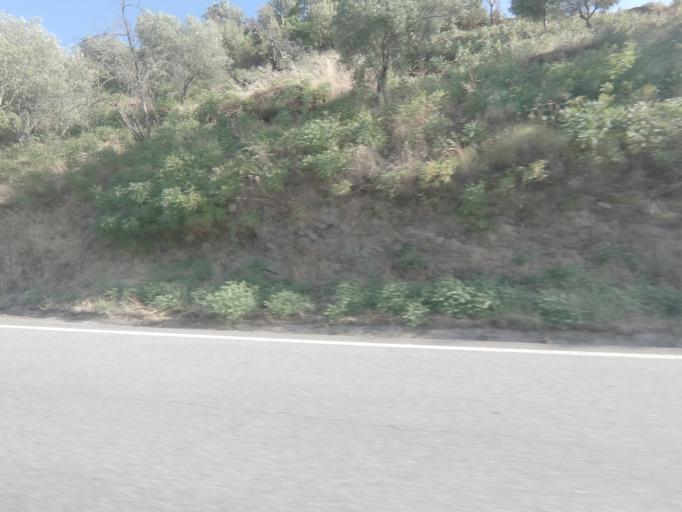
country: PT
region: Viseu
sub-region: Tabuaco
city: Tabuaco
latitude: 41.1593
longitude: -7.6129
